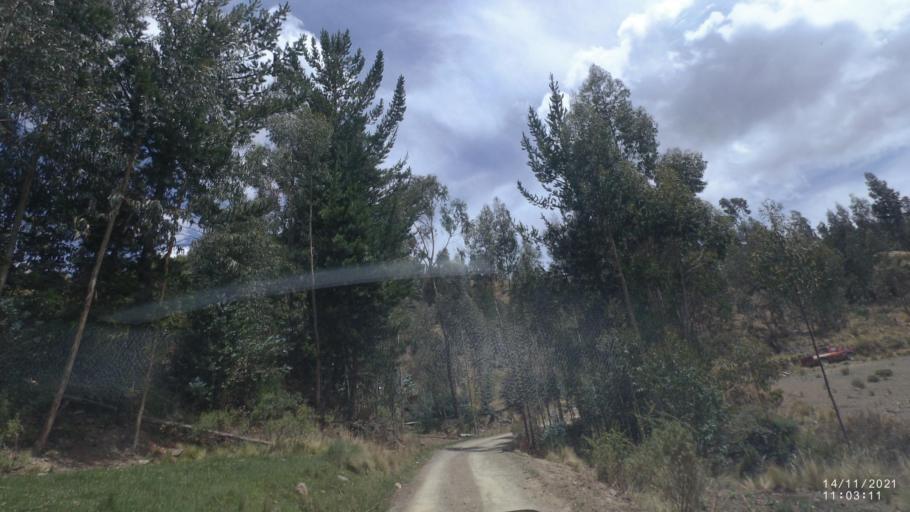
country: BO
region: Cochabamba
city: Cochabamba
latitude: -17.3373
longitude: -66.0601
